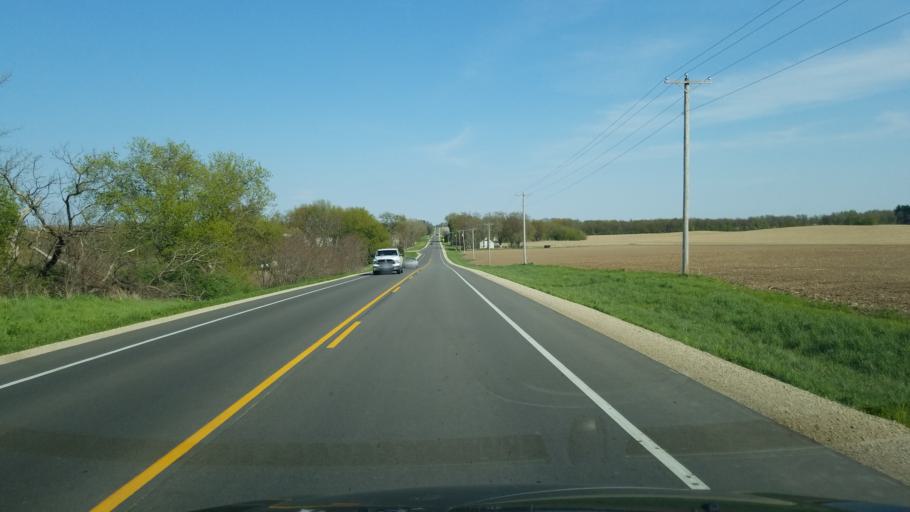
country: US
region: Wisconsin
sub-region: Dane County
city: Fitchburg
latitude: 42.9610
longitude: -89.4803
